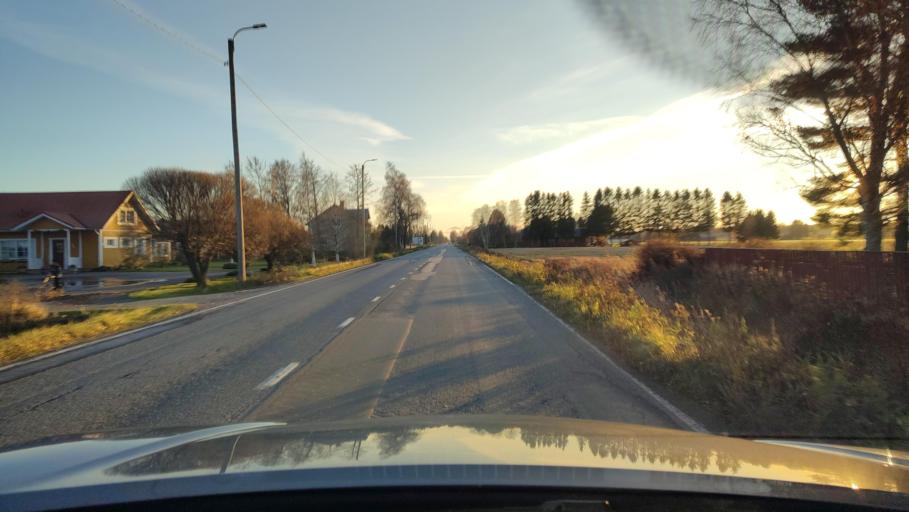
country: FI
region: Ostrobothnia
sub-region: Sydosterbotten
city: Naerpes
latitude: 62.5403
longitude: 21.3916
